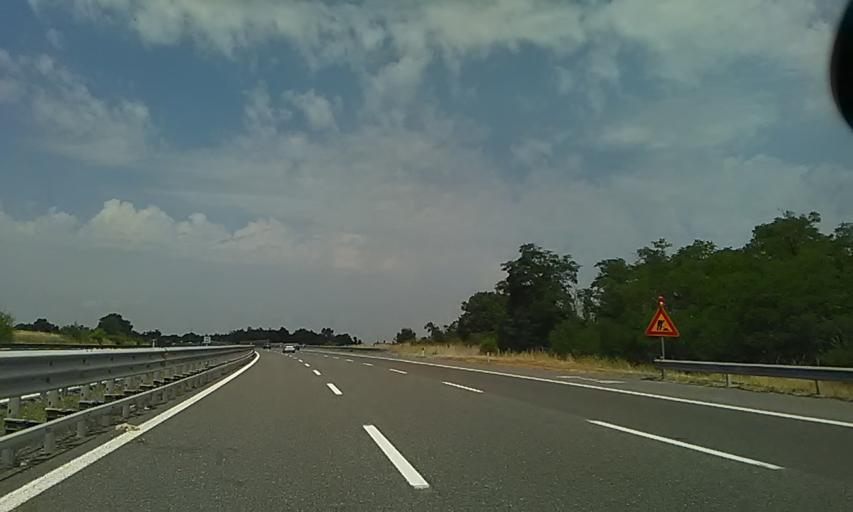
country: IT
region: Piedmont
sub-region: Provincia di Alessandria
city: Capriata d'Orba
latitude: 44.7238
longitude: 8.6670
